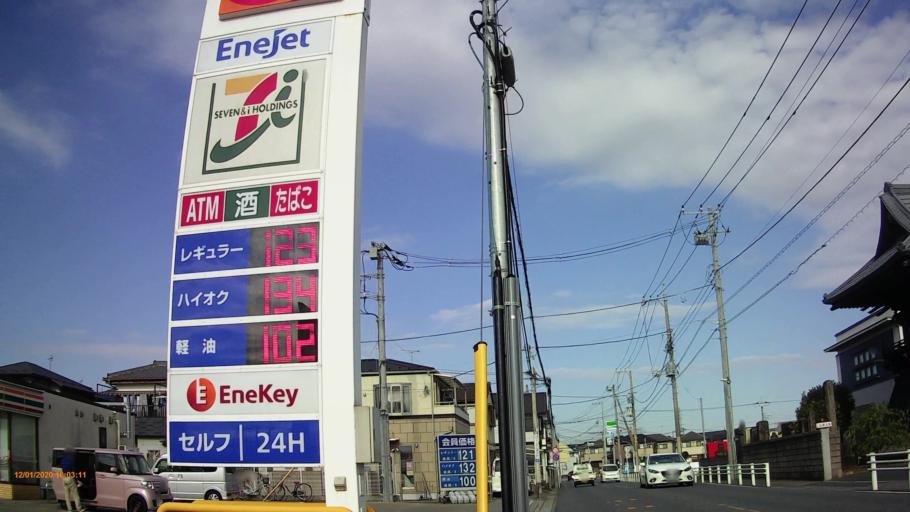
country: JP
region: Chiba
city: Yotsukaido
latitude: 35.6363
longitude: 140.1643
